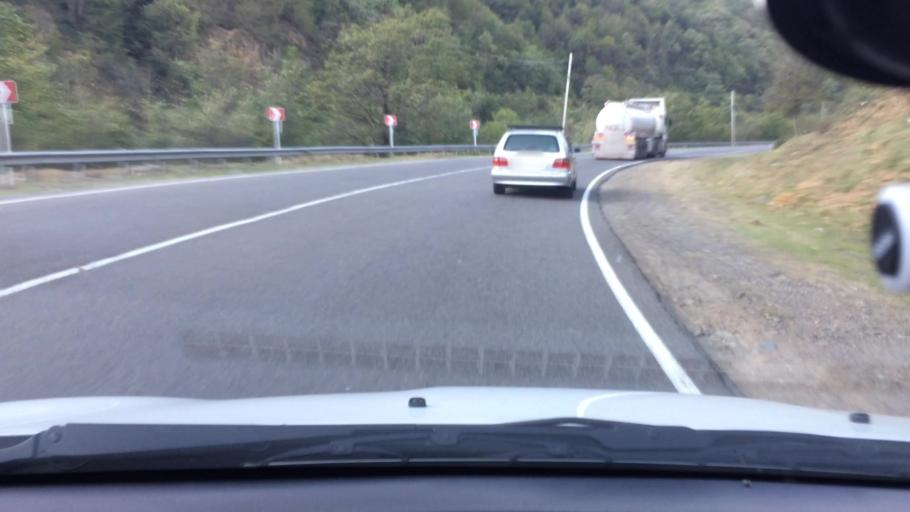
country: GE
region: Imereti
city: Kharagauli
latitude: 42.1056
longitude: 43.2470
